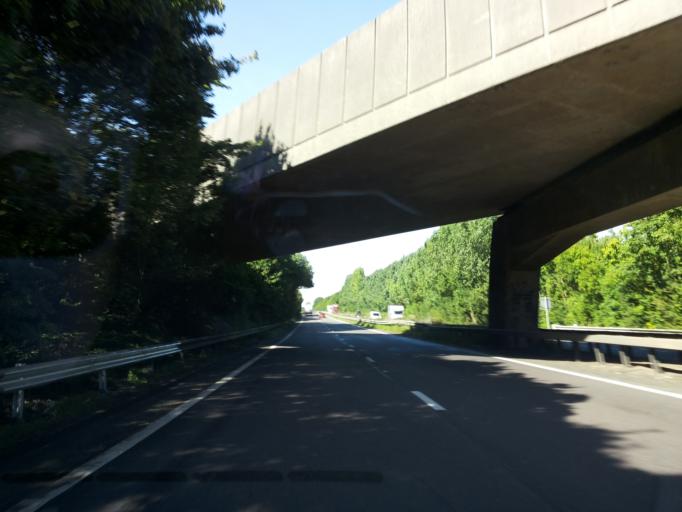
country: GB
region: England
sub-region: Kent
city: Canterbury
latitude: 51.2755
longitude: 1.0504
